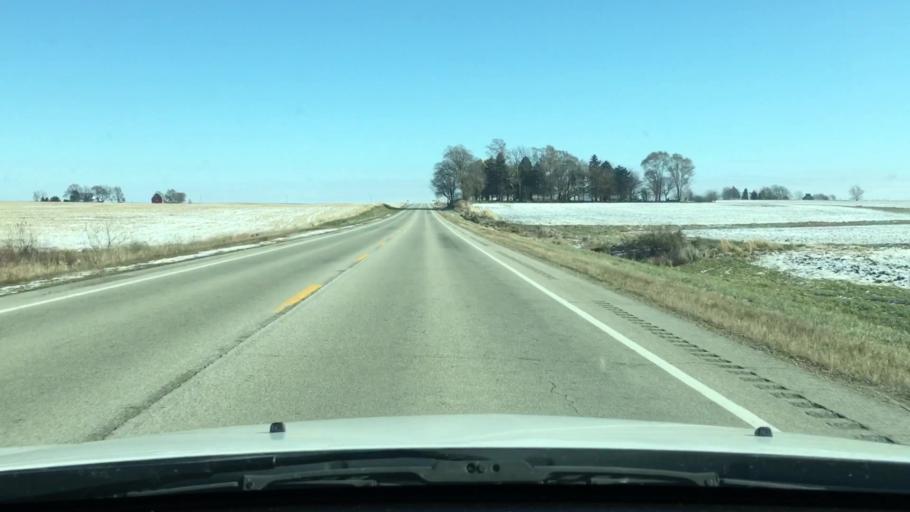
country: US
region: Illinois
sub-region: DeKalb County
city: Malta
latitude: 42.0010
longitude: -88.8886
